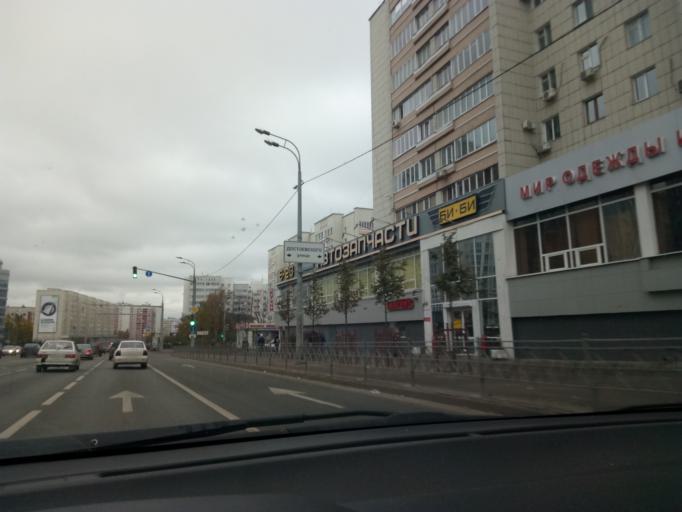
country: RU
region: Tatarstan
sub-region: Gorod Kazan'
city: Kazan
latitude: 55.7887
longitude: 49.1517
